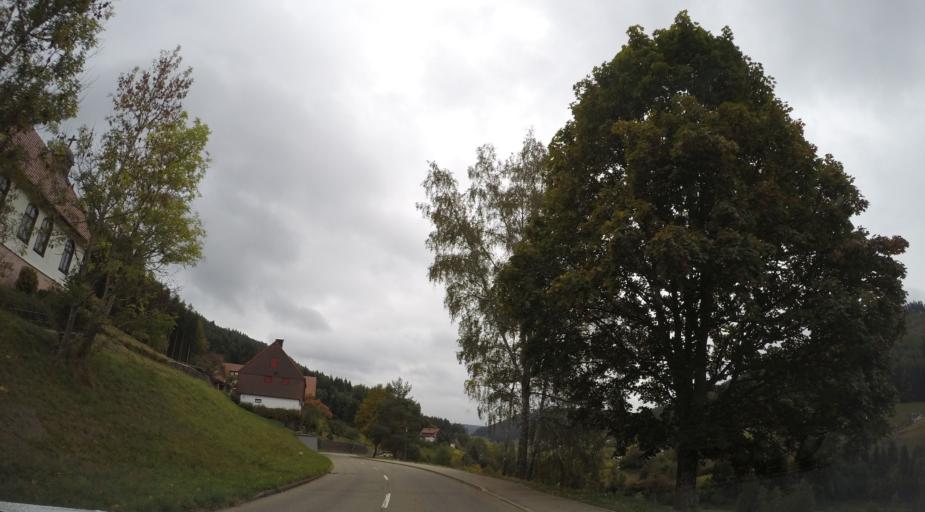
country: DE
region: Baden-Wuerttemberg
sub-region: Karlsruhe Region
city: Baiersbronn
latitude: 48.5352
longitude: 8.3595
